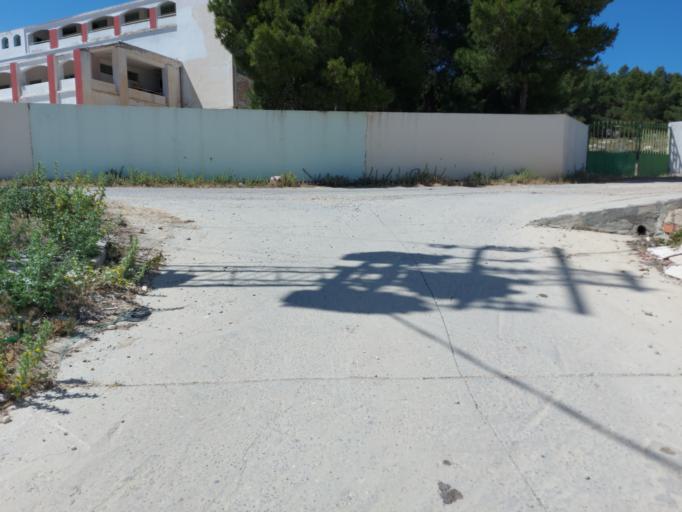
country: TN
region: Kef
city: El Kef
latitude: 36.1836
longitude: 8.7288
